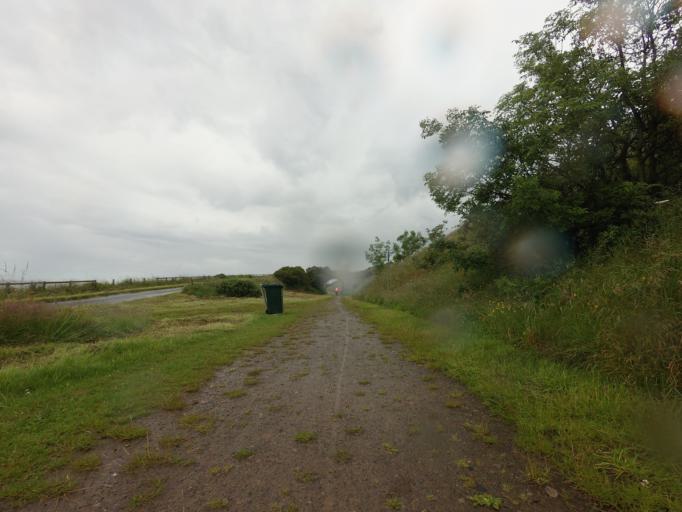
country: GB
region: Scotland
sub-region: Moray
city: Buckie
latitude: 57.6654
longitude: -3.0057
